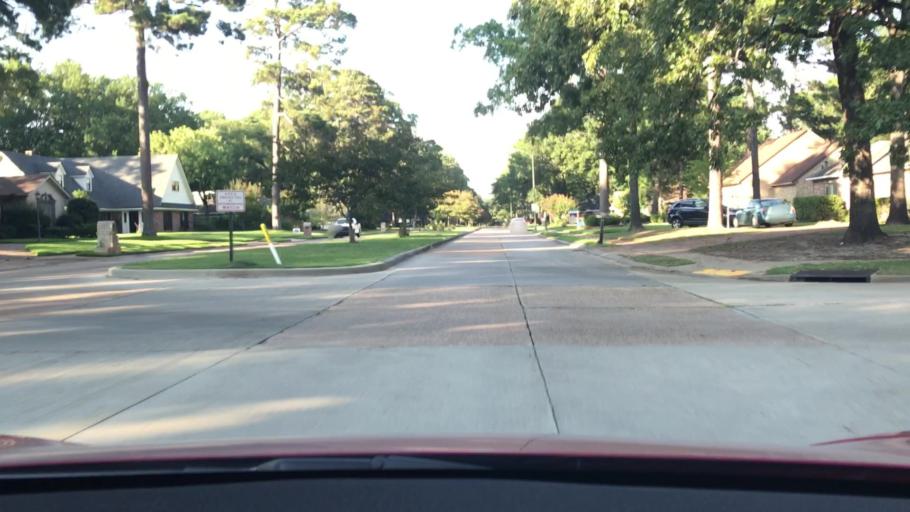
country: US
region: Louisiana
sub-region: Bossier Parish
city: Bossier City
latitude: 32.4259
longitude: -93.7388
